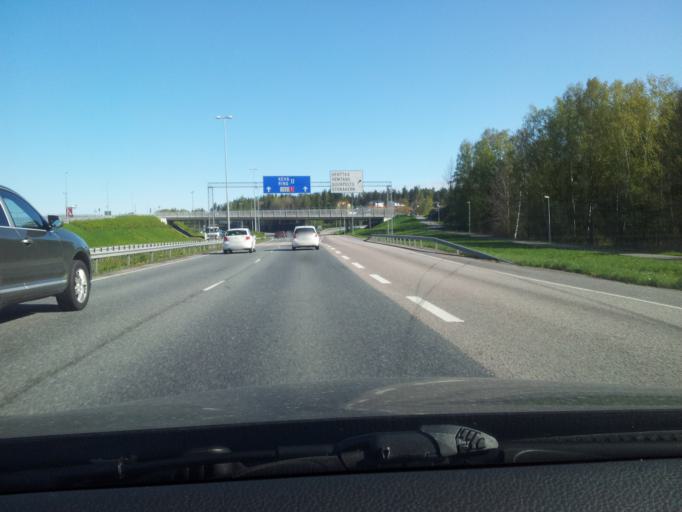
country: FI
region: Uusimaa
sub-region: Helsinki
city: Kauniainen
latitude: 60.1857
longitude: 24.7491
